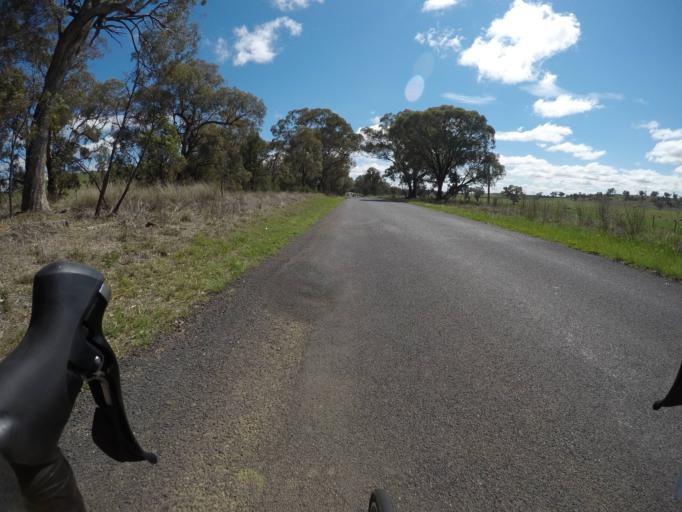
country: AU
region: New South Wales
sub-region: Dubbo Municipality
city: Dubbo
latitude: -32.5441
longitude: 148.5458
